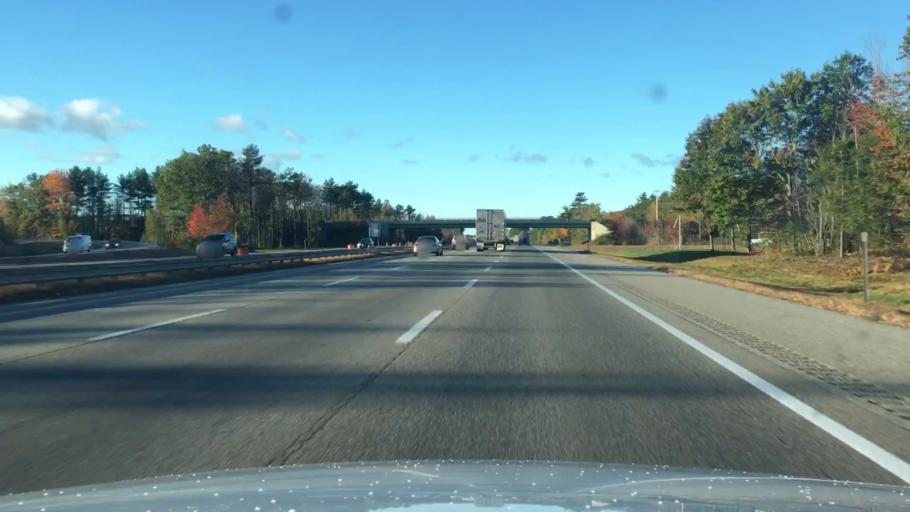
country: US
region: Maine
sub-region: Cumberland County
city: West Scarborough
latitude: 43.6071
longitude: -70.3705
